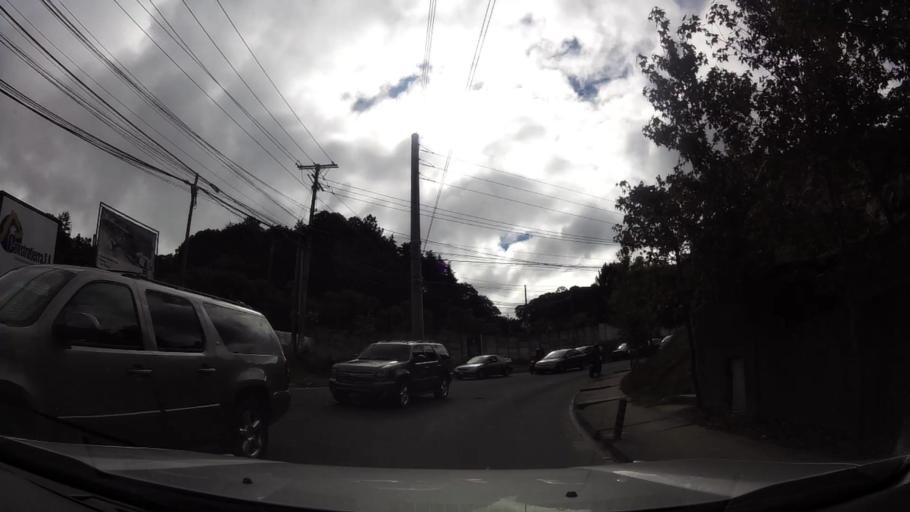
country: GT
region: Guatemala
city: Santa Catarina Pinula
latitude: 14.5692
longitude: -90.4851
